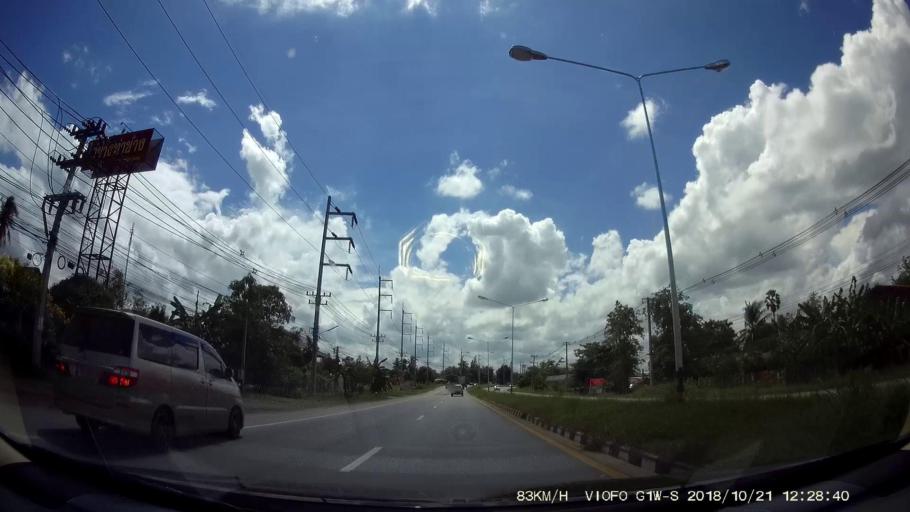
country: TH
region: Nakhon Ratchasima
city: Dan Khun Thot
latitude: 15.1868
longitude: 101.7589
